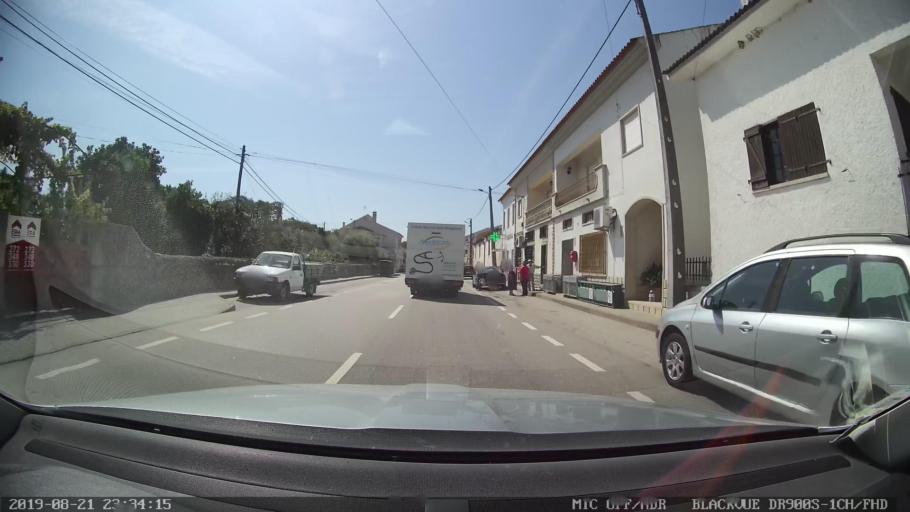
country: PT
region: Guarda
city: Alcains
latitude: 39.8827
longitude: -7.3970
